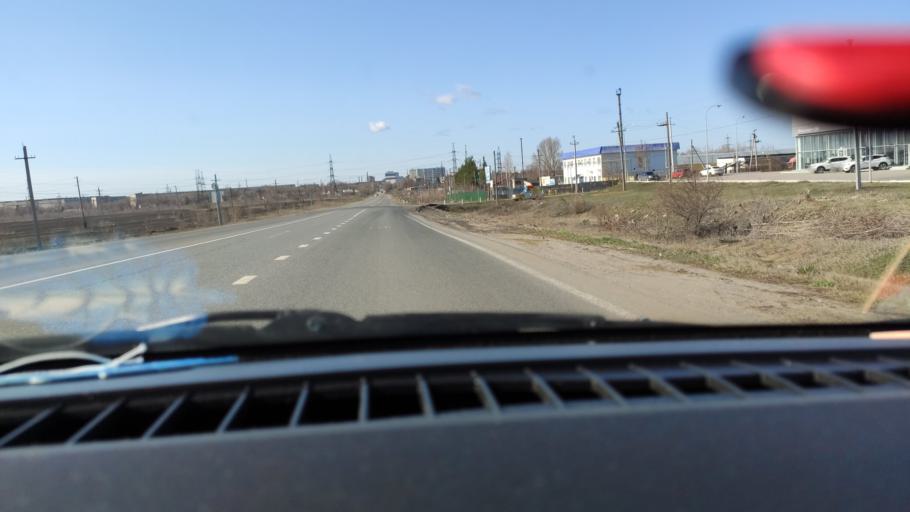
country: RU
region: Samara
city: Syzran'
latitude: 53.2011
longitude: 48.5092
